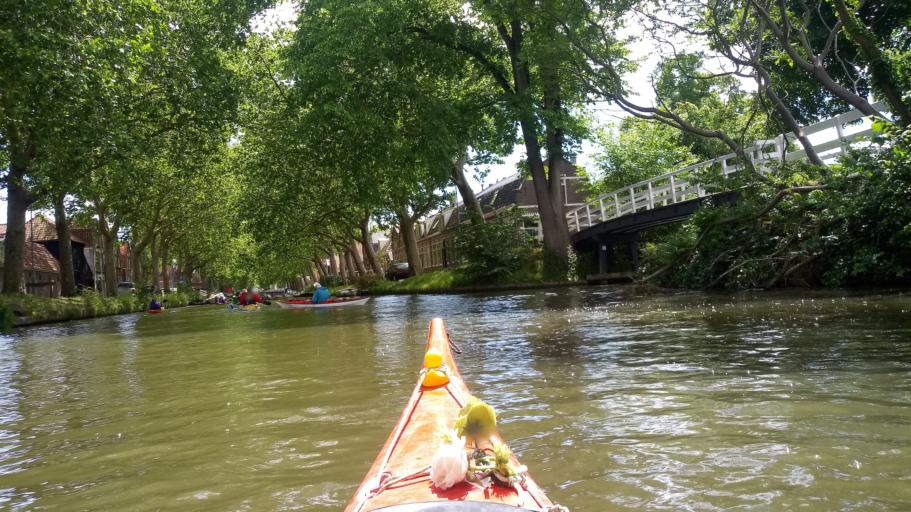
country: NL
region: North Holland
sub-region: Gemeente Enkhuizen
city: Enkhuizen
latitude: 52.7066
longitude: 5.2846
